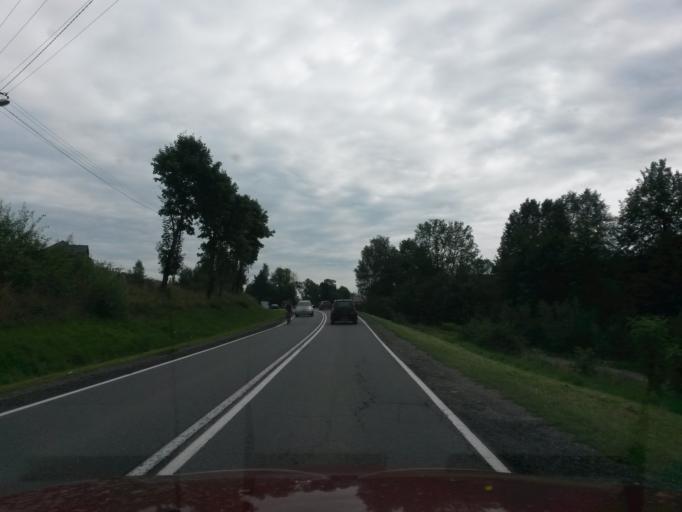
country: PL
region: Lesser Poland Voivodeship
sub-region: Powiat nowosadecki
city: Labowa
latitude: 49.5188
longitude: 20.8796
